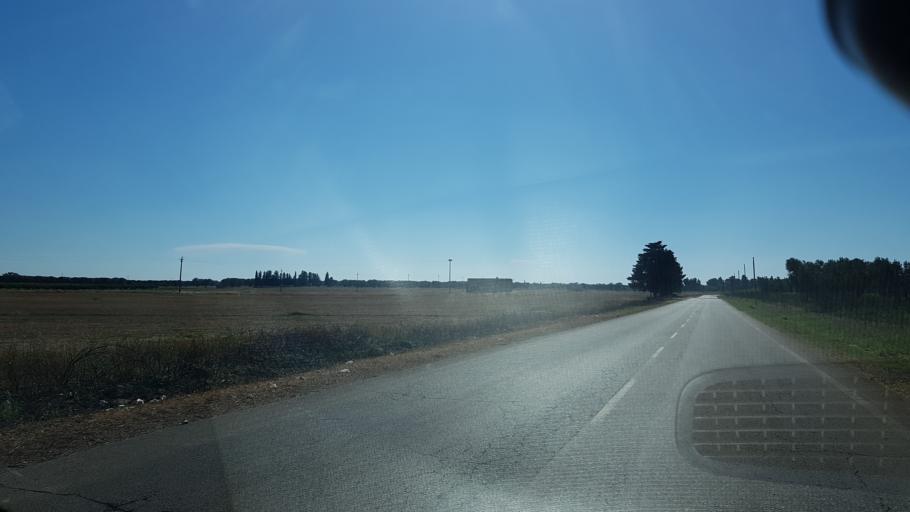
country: IT
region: Apulia
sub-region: Provincia di Brindisi
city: Mesagne
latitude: 40.5566
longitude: 17.8550
